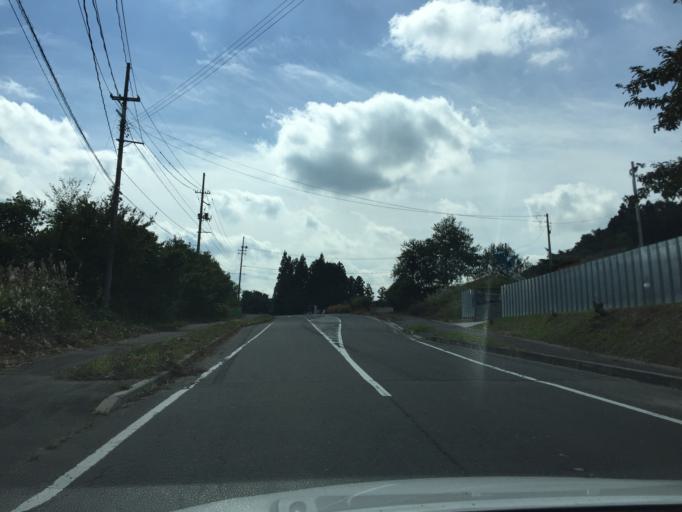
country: JP
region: Fukushima
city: Miharu
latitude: 37.4411
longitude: 140.5177
